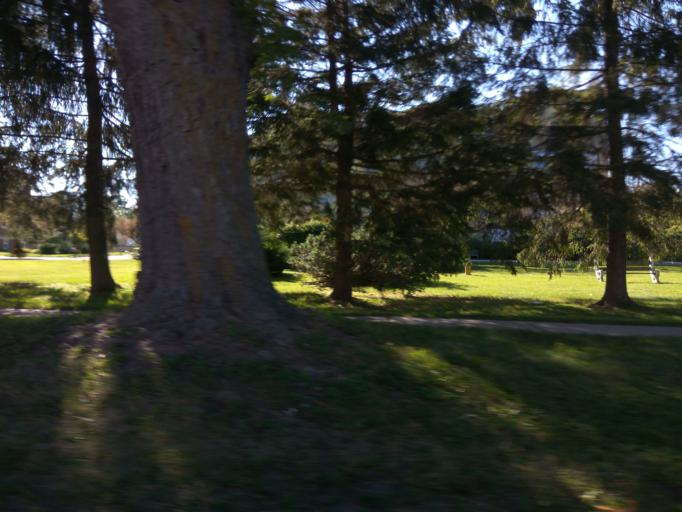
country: CA
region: Ontario
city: Stratford
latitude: 43.3685
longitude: -80.9970
